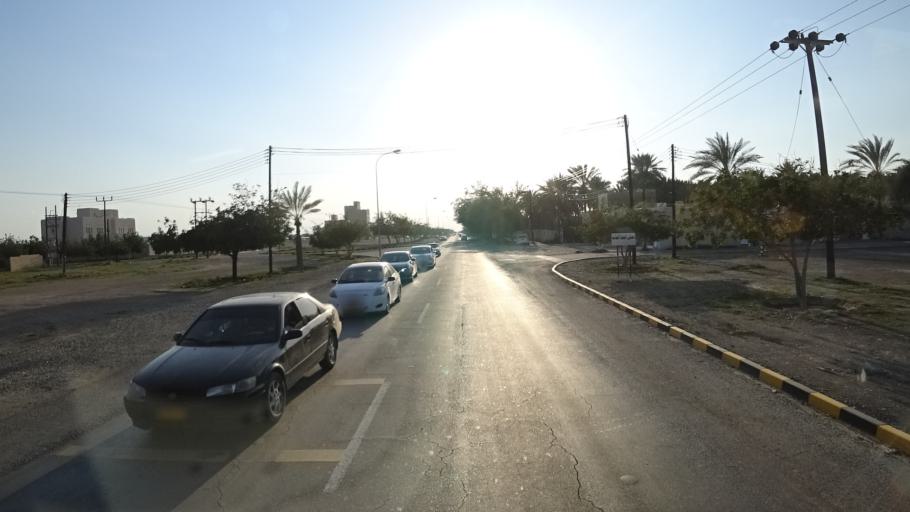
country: OM
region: Al Batinah
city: Al Khaburah
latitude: 23.9665
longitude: 57.0836
